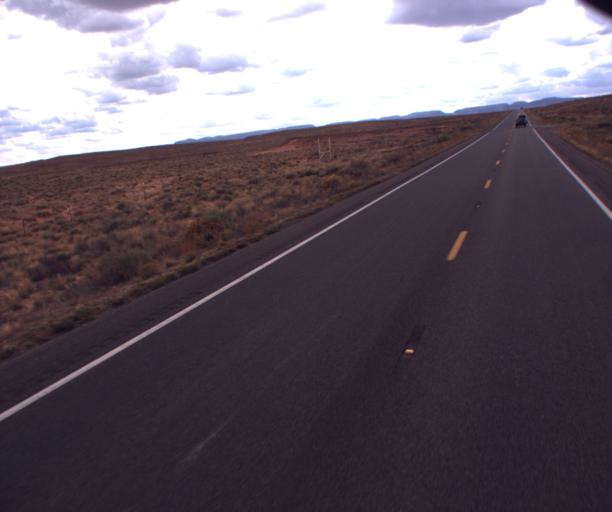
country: US
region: Arizona
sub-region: Navajo County
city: Kayenta
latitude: 36.7460
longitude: -110.0707
